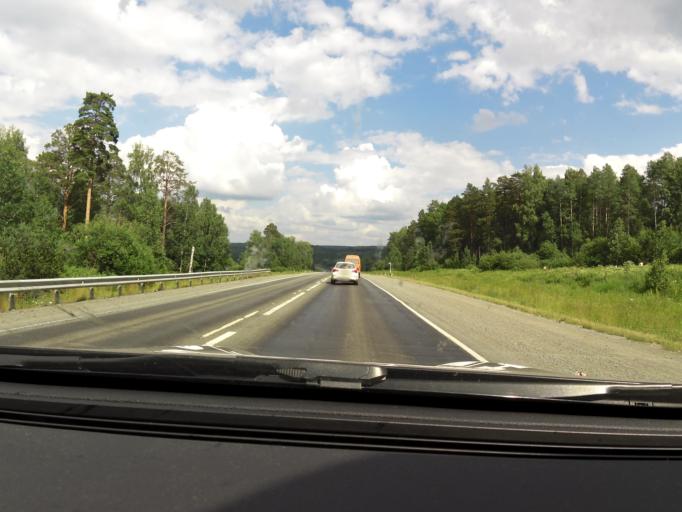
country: RU
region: Sverdlovsk
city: Bisert'
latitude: 56.8322
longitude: 58.8251
